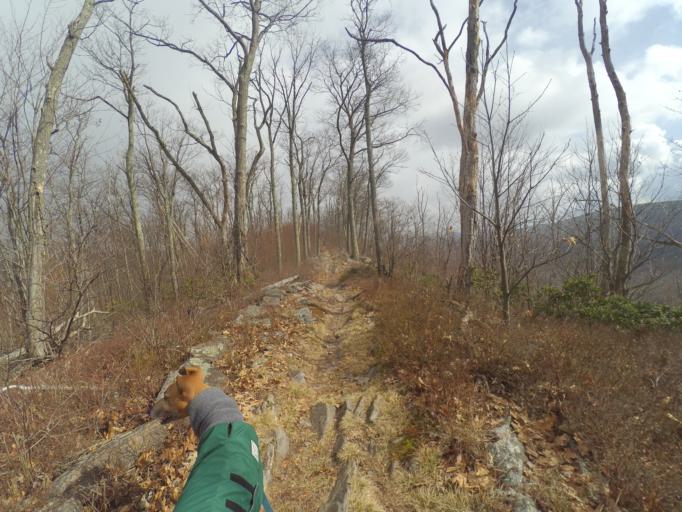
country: US
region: Pennsylvania
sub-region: Centre County
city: Boalsburg
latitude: 40.7510
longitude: -77.7326
